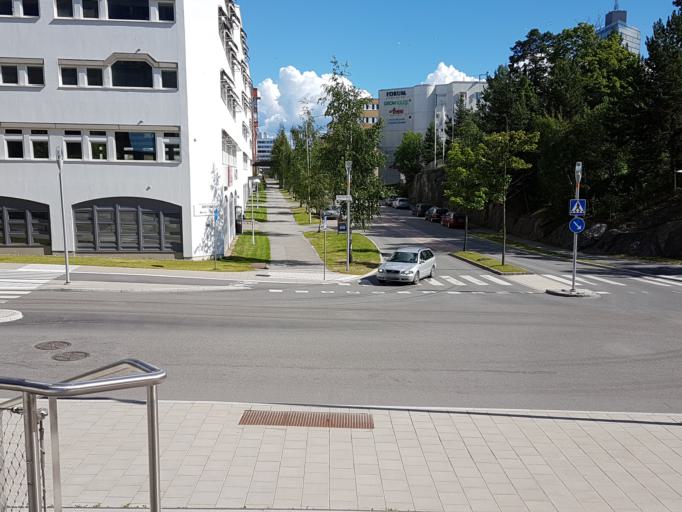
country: SE
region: Stockholm
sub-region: Stockholms Kommun
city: Kista
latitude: 59.4066
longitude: 17.9452
